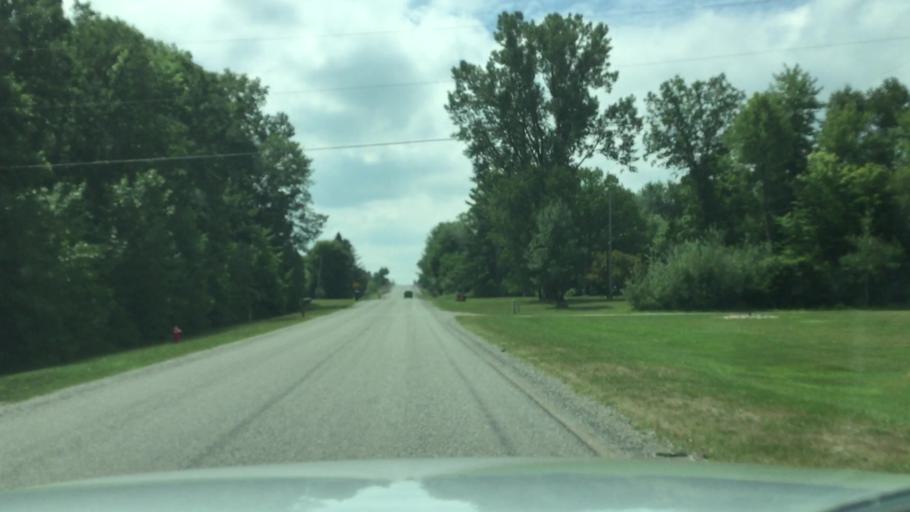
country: US
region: Michigan
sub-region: Saginaw County
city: Birch Run
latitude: 43.2737
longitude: -83.7944
